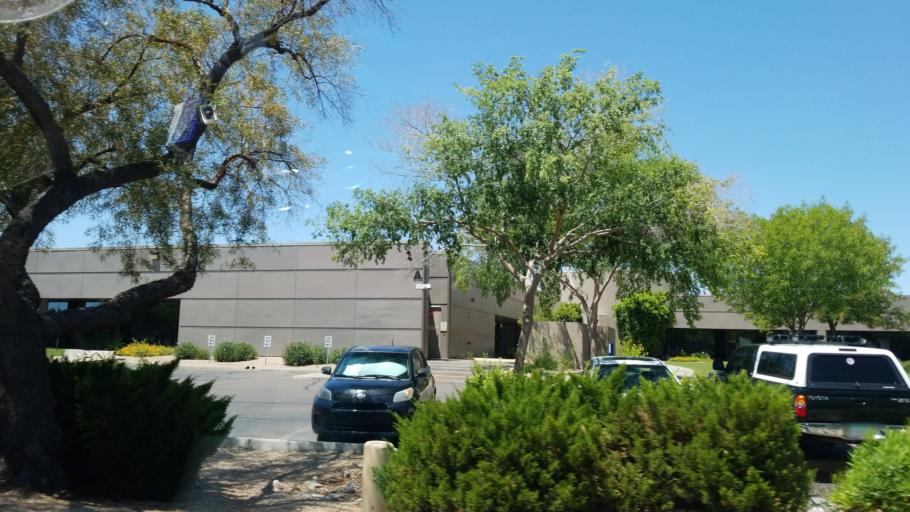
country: US
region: Arizona
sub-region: Maricopa County
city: Glendale
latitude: 33.6310
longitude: -112.1183
